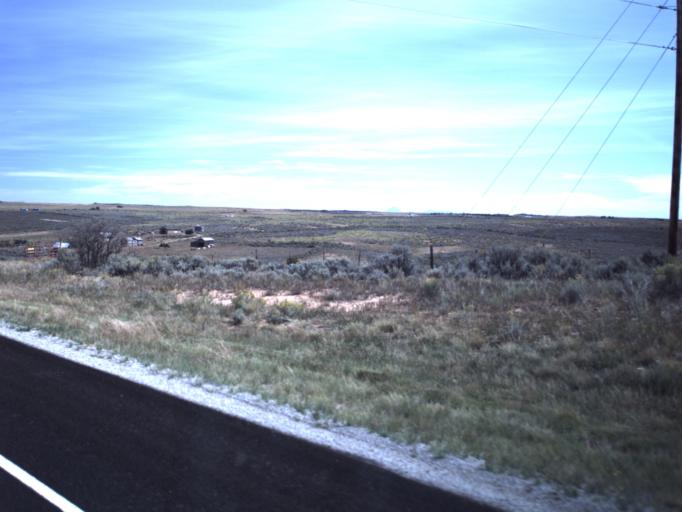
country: US
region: Utah
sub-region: San Juan County
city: Monticello
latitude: 37.8712
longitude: -109.2565
